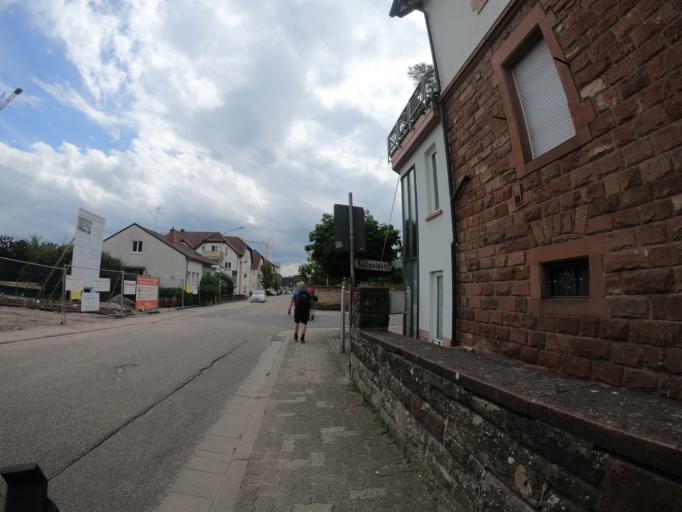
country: DE
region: Rheinland-Pfalz
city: Bad Bergzabern
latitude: 49.1044
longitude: 7.9992
